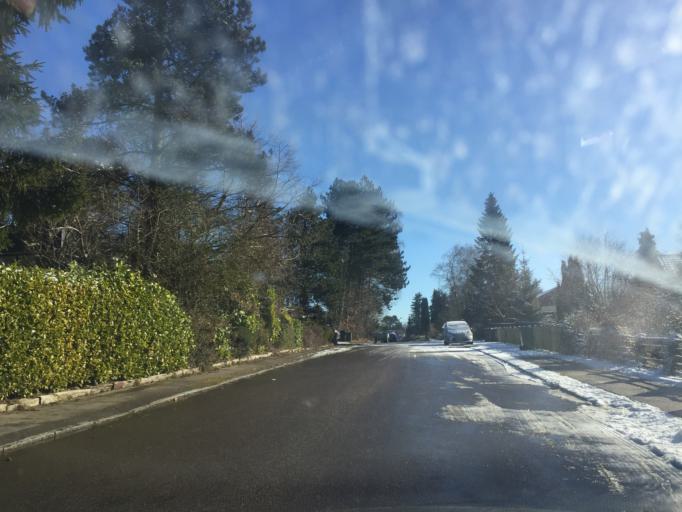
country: DK
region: Capital Region
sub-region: Herlev Kommune
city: Herlev
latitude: 55.7567
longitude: 12.4239
